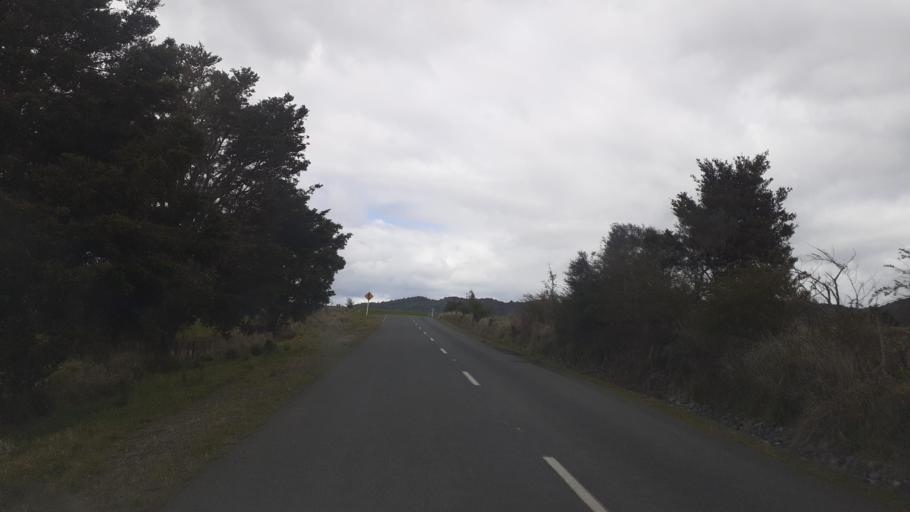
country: NZ
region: Northland
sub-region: Far North District
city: Moerewa
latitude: -35.5894
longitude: 173.9746
